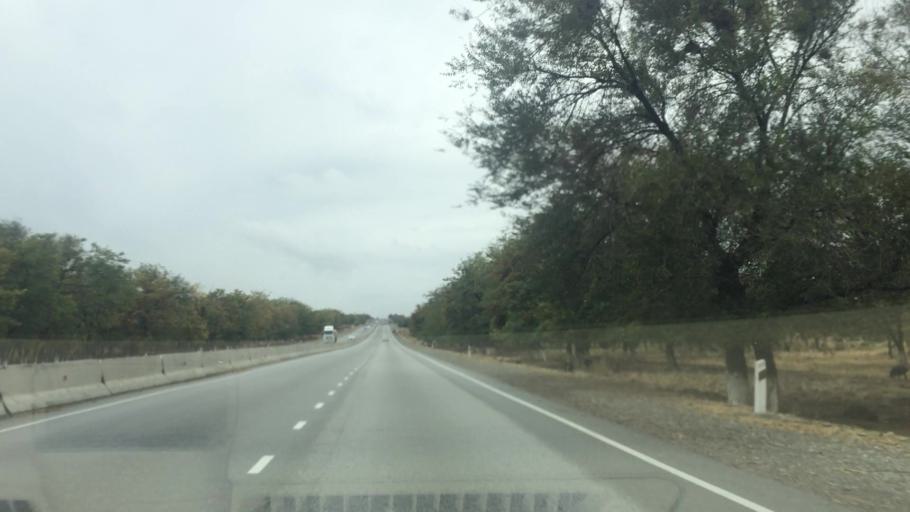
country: UZ
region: Samarqand
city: Bulung'ur
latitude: 39.8700
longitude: 67.4774
